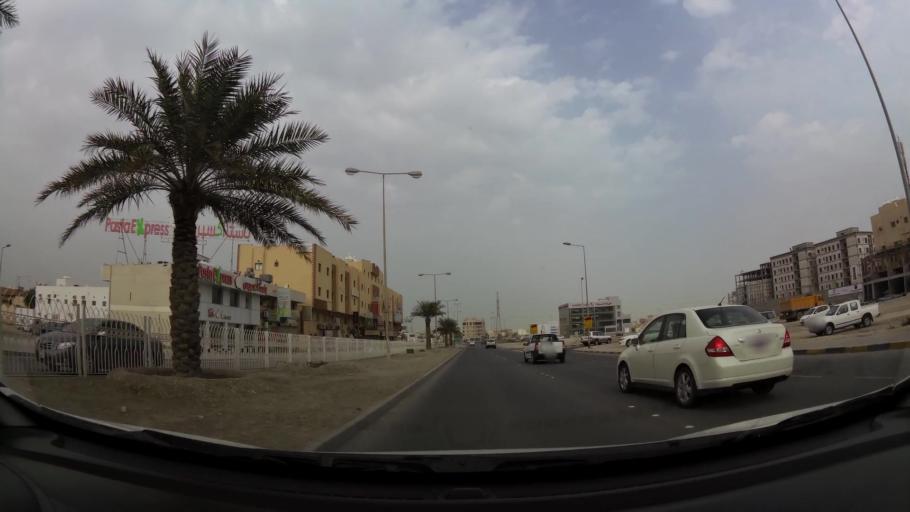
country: BH
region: Northern
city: Ar Rifa'
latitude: 26.1397
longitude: 50.5777
